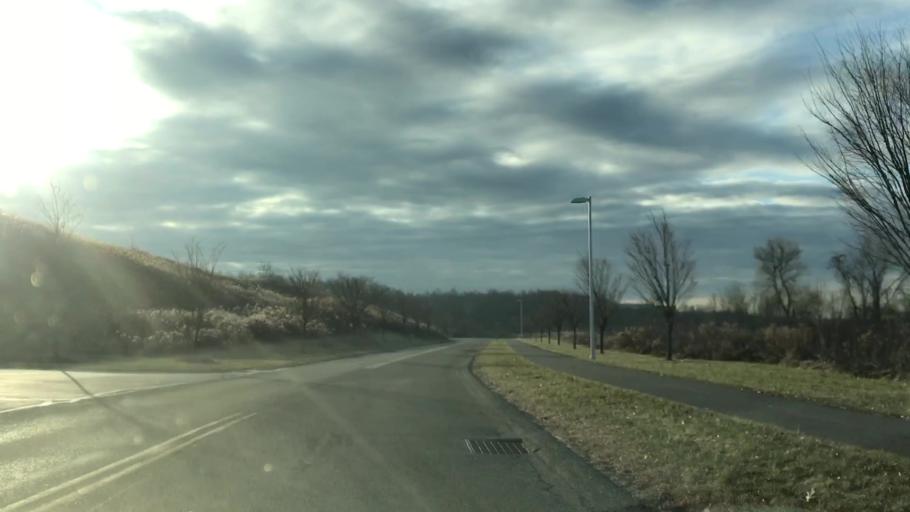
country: US
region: Pennsylvania
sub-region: Allegheny County
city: Carnot-Moon
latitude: 40.4892
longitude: -80.1964
